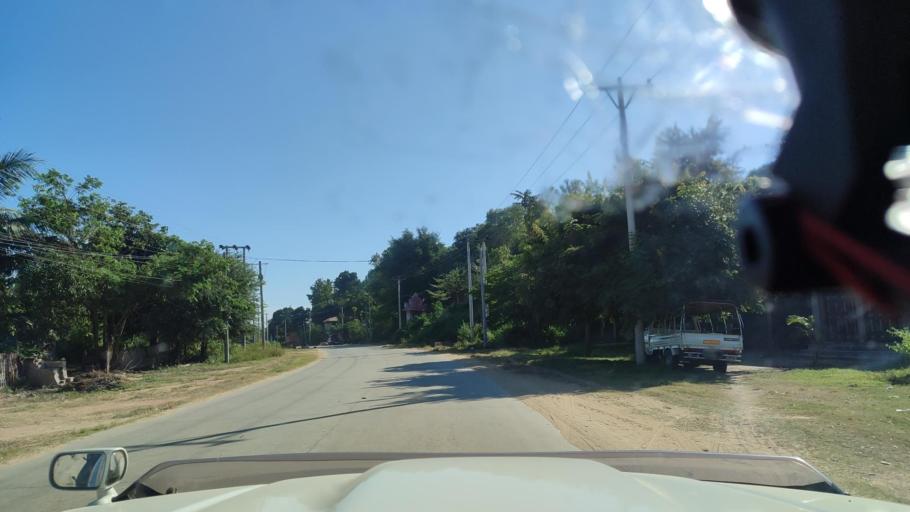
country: MM
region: Mandalay
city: Nay Pyi Taw
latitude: 19.9124
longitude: 96.0237
